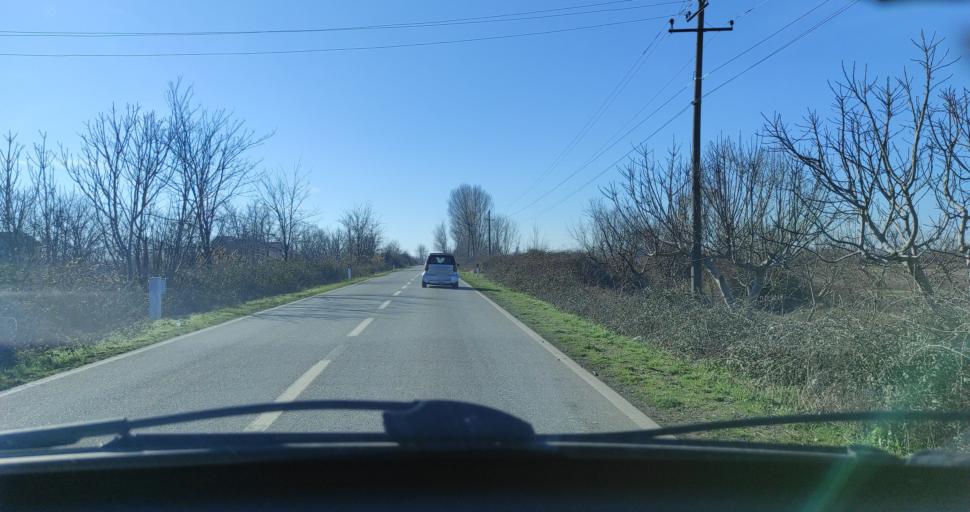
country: AL
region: Shkoder
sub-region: Rrethi i Shkodres
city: Velipoje
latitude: 41.8987
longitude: 19.4030
